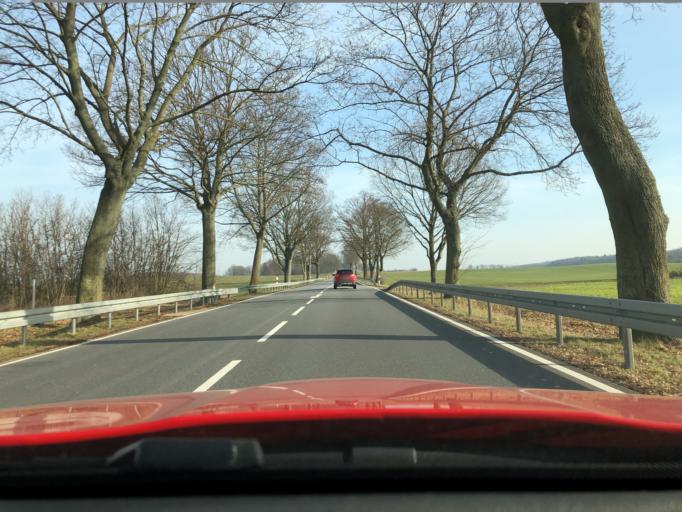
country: DE
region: Brandenburg
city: Muncheberg
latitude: 52.5048
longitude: 14.1902
